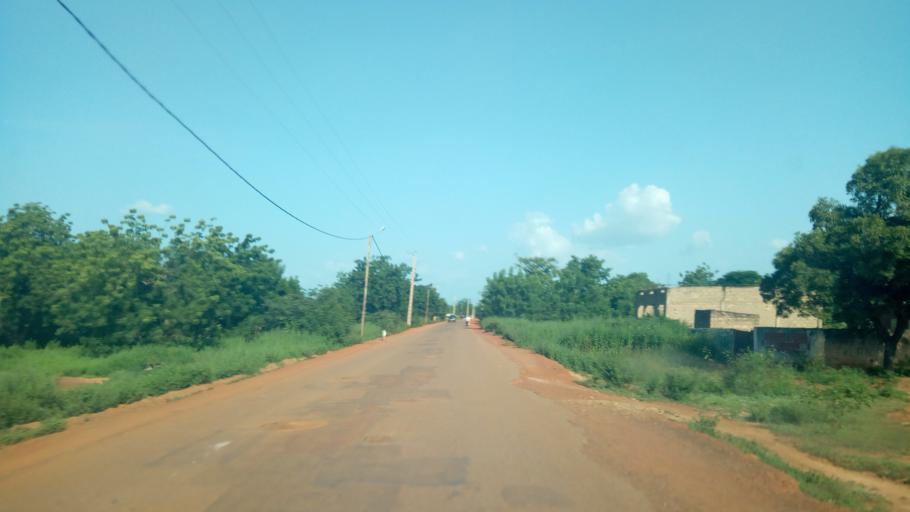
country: ML
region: Sikasso
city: Yorosso
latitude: 12.1848
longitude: -4.8143
